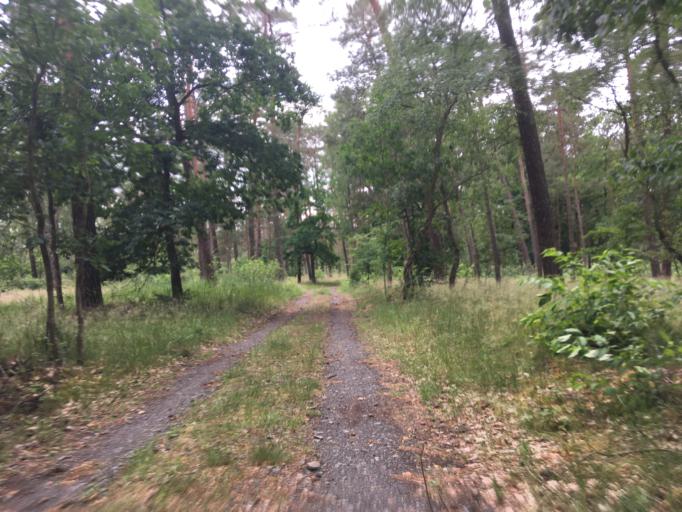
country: DE
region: Berlin
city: Rahnsdorf
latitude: 52.4165
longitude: 13.6981
